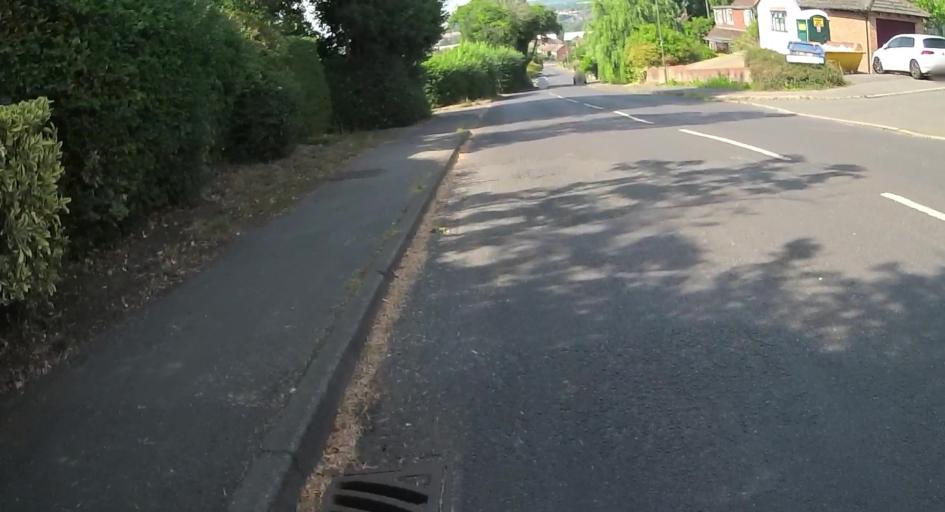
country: GB
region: England
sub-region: Surrey
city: Farnham
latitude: 51.2002
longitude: -0.8064
